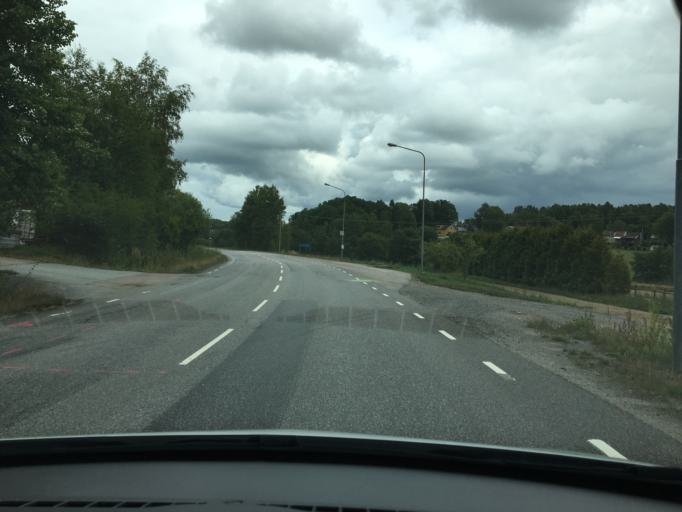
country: SE
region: Vaestra Goetaland
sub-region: Ale Kommun
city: Alafors
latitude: 57.9206
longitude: 12.0922
